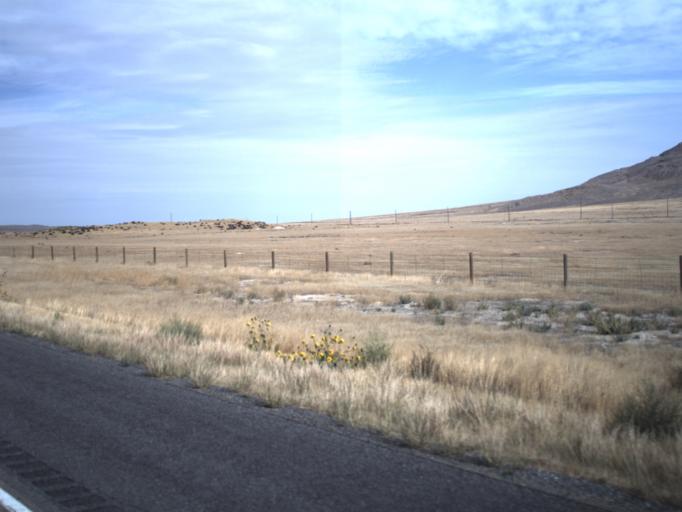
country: US
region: Utah
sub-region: Tooele County
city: Grantsville
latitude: 40.7929
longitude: -112.8361
